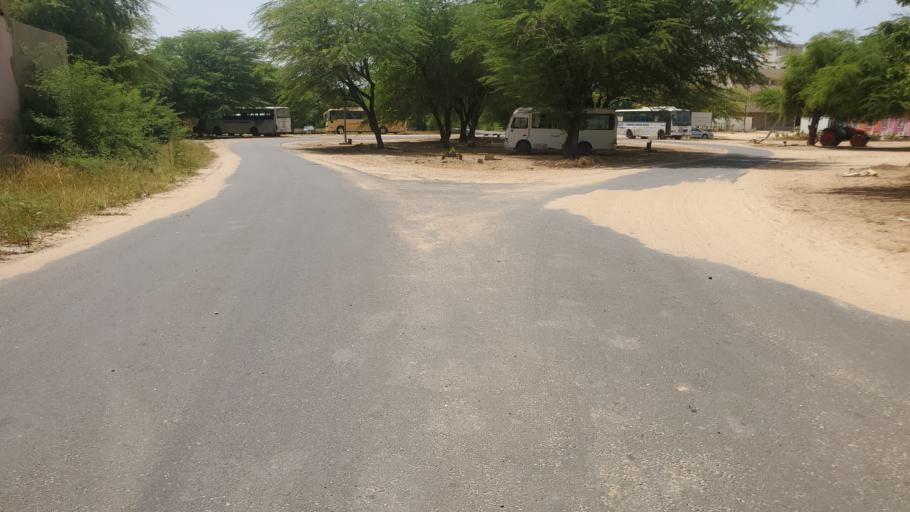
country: SN
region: Saint-Louis
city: Saint-Louis
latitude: 16.0604
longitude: -16.4234
